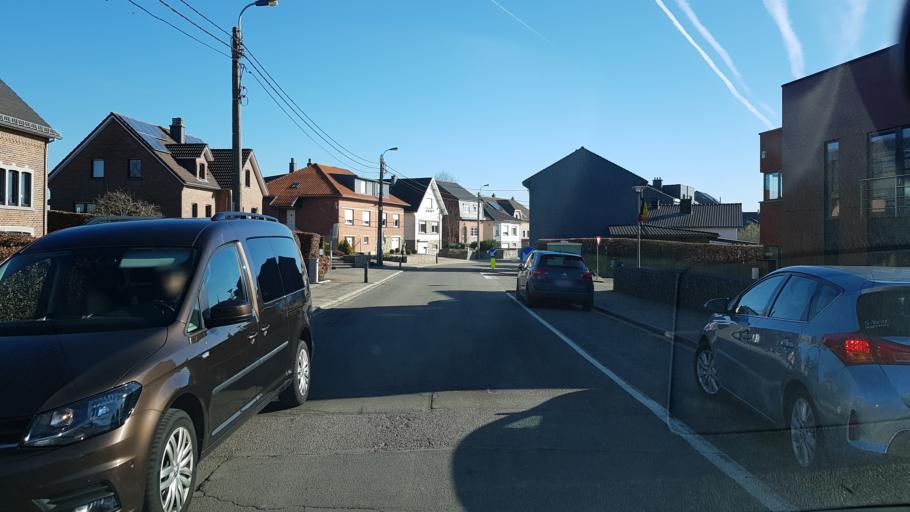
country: BE
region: Wallonia
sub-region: Province de Liege
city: Welkenraedt
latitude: 50.6601
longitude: 5.9581
